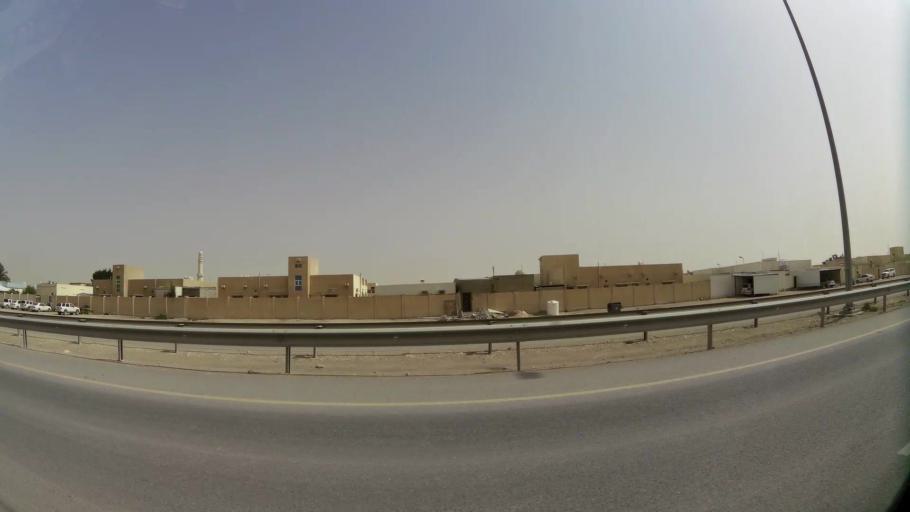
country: QA
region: Baladiyat ar Rayyan
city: Ar Rayyan
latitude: 25.1962
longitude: 51.3616
